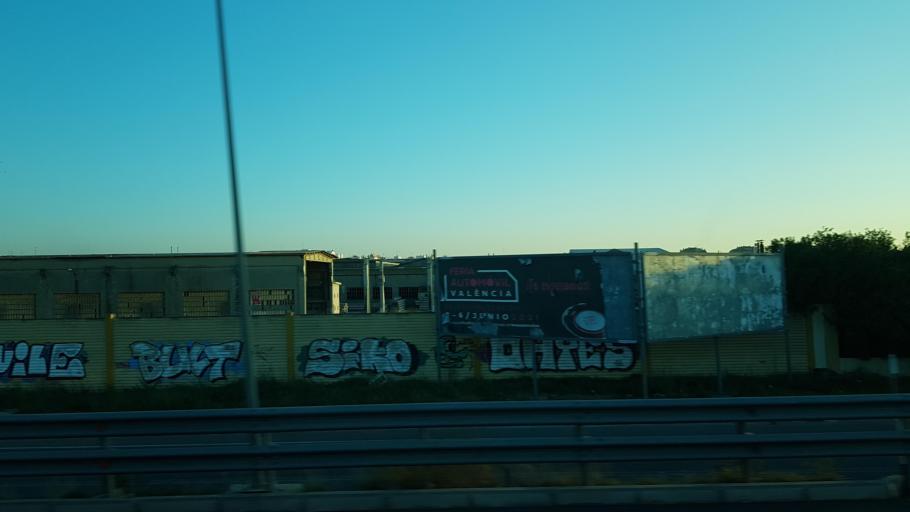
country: ES
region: Valencia
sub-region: Provincia de Valencia
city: Manises
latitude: 39.4804
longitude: -0.4641
